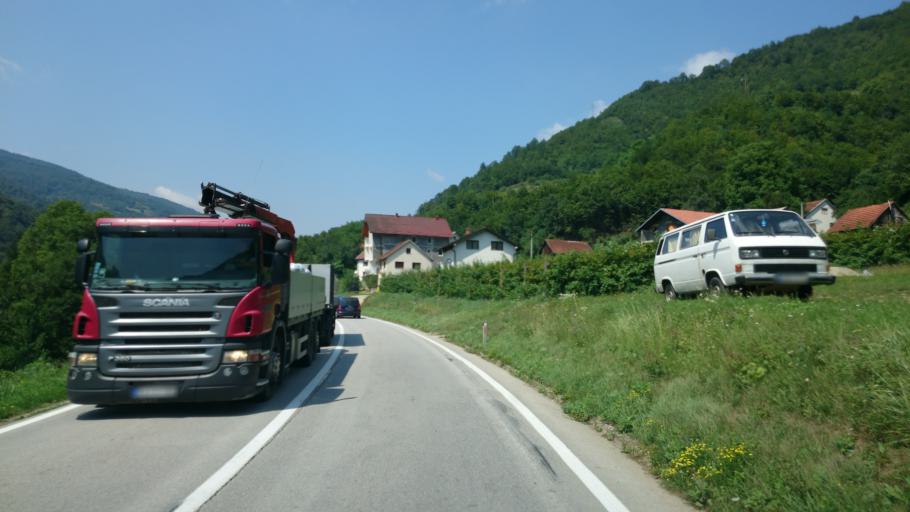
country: BA
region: Federation of Bosnia and Herzegovina
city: Donji Vakuf
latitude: 44.1729
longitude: 17.3602
